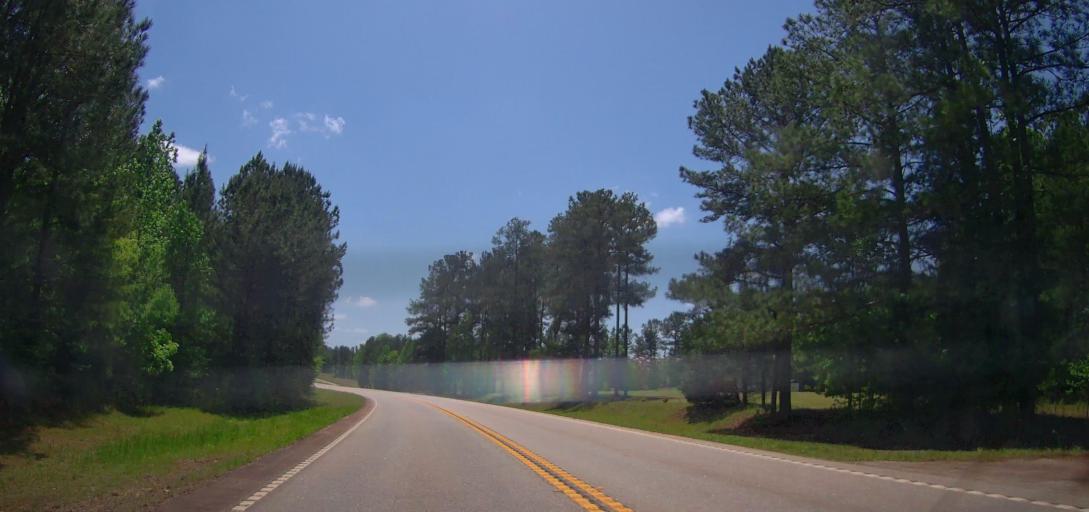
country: US
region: Georgia
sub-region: Jasper County
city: Monticello
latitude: 33.2437
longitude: -83.6805
